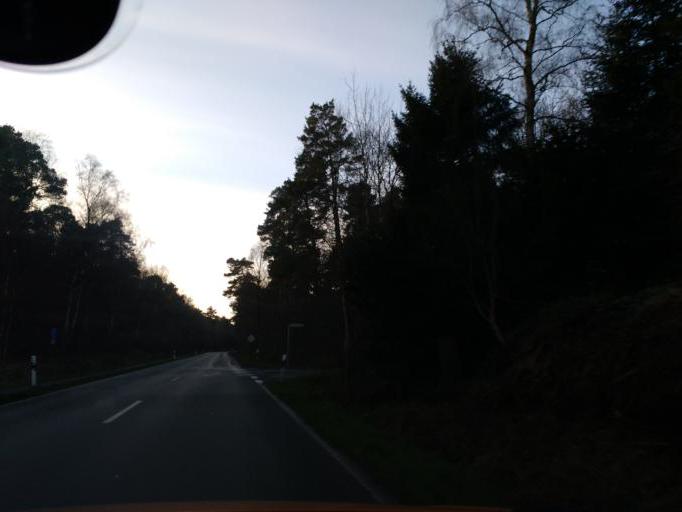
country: DE
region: Lower Saxony
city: Hude
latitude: 53.0969
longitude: 8.4159
